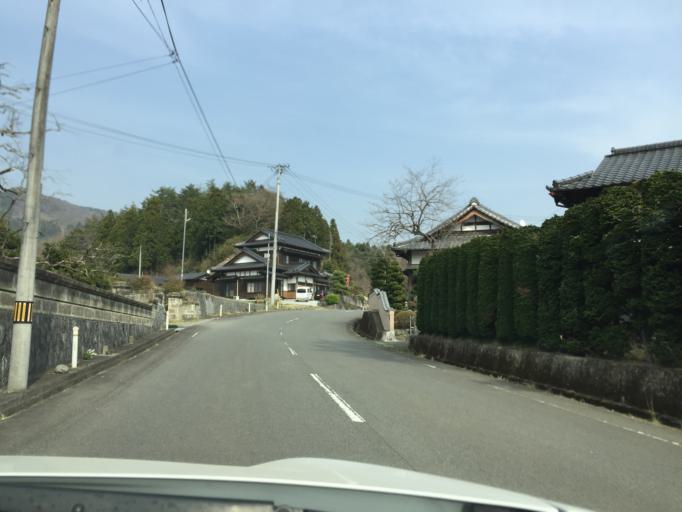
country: JP
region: Fukushima
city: Iwaki
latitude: 37.0294
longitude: 140.7380
